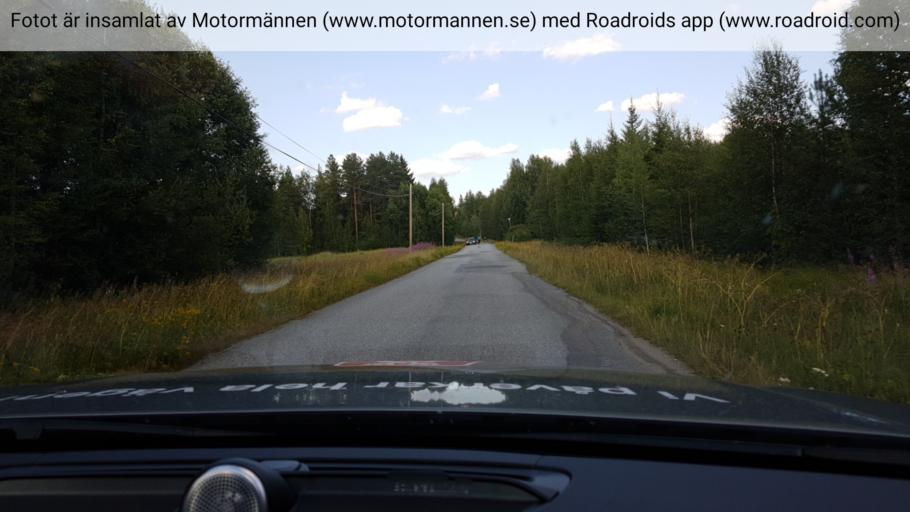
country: SE
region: Vaesterbotten
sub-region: Dorotea Kommun
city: Dorotea
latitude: 63.9180
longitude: 16.3308
